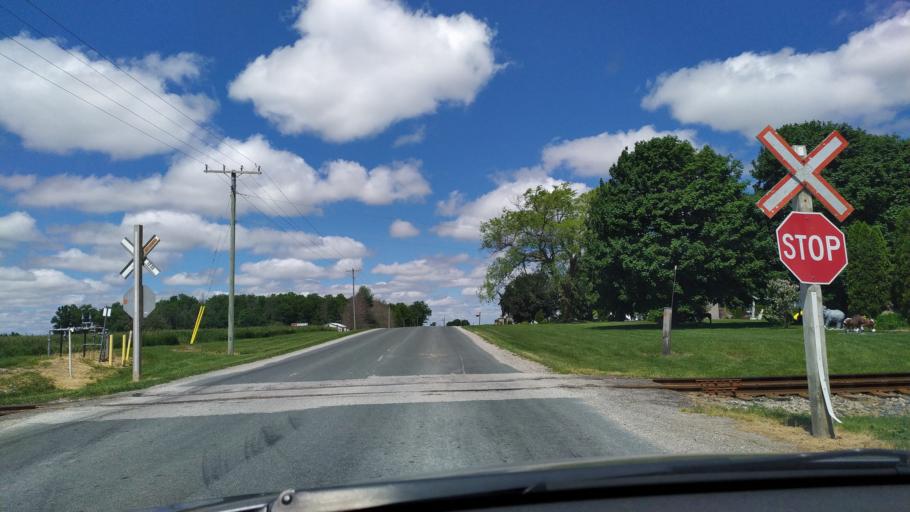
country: CA
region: Ontario
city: Huron East
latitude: 43.4541
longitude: -81.1801
